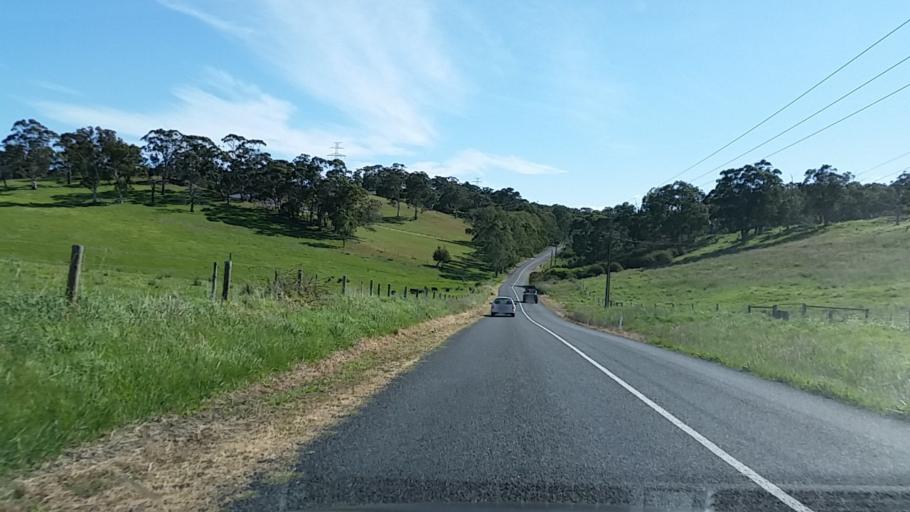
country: AU
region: South Australia
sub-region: Mount Barker
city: Little Hampton
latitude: -35.0777
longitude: 138.8328
